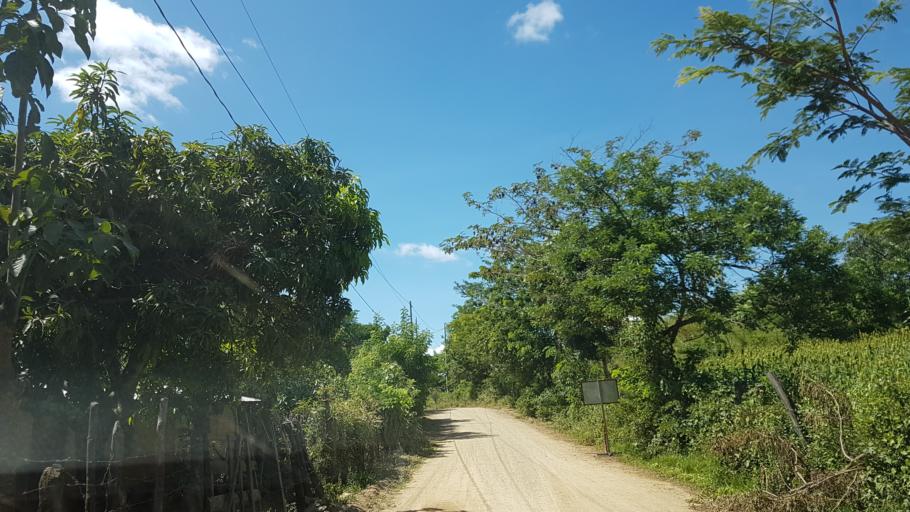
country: HN
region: El Paraiso
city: Santa Cruz
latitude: 13.7331
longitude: -86.6868
